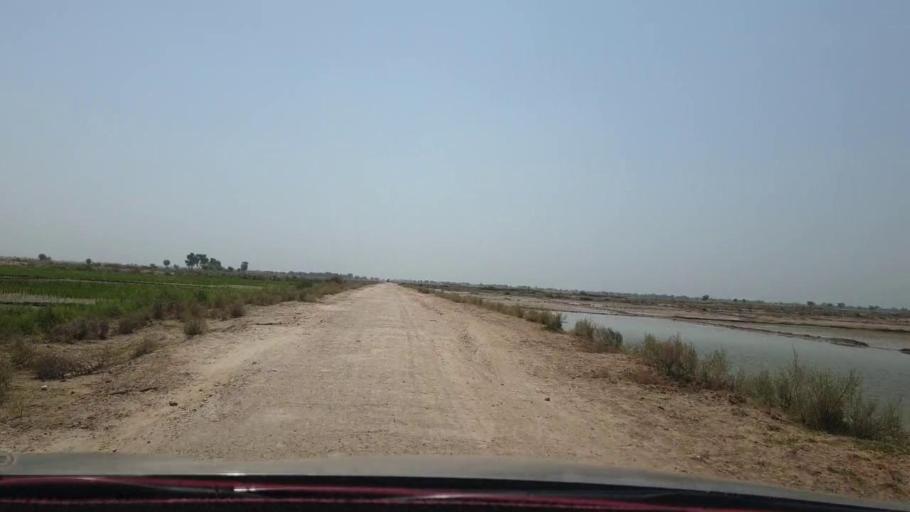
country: PK
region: Sindh
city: Kambar
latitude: 27.5850
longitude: 67.8764
